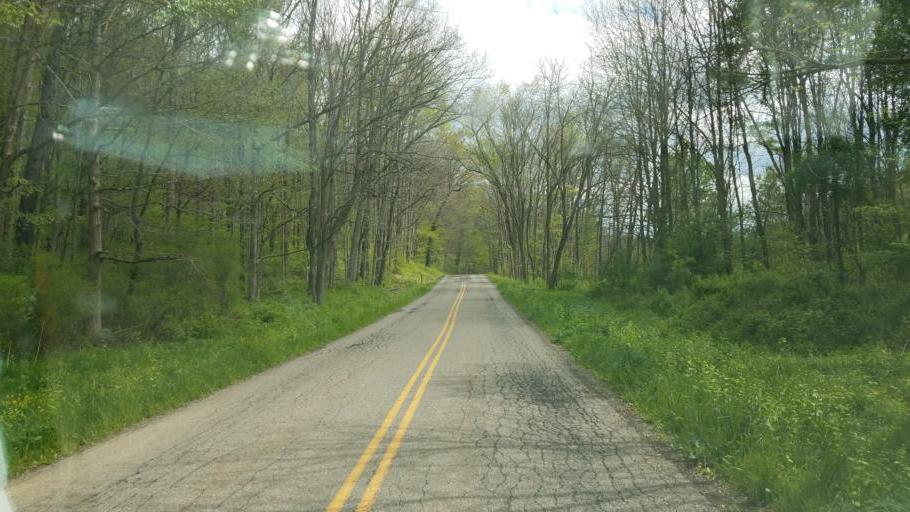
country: US
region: Ohio
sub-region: Knox County
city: Danville
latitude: 40.5420
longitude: -82.2869
